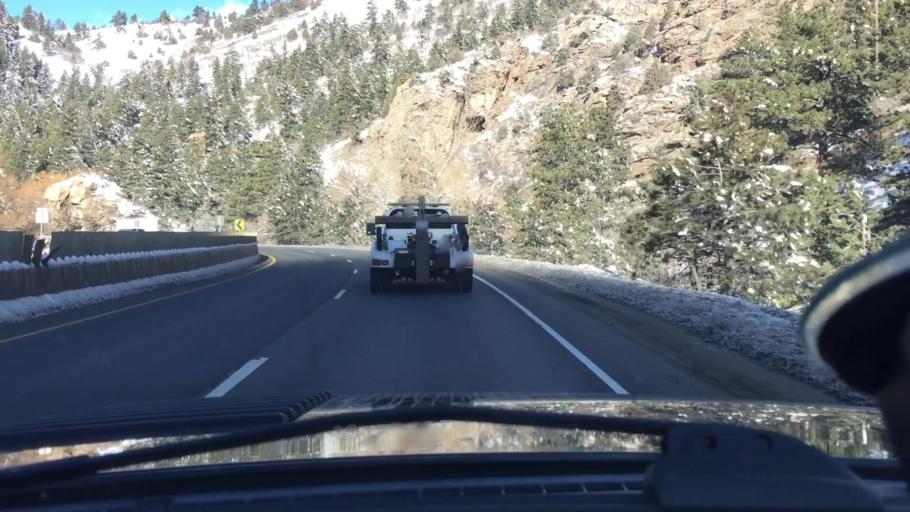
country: US
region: Colorado
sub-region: Jefferson County
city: Indian Hills
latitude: 39.6193
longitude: -105.2259
